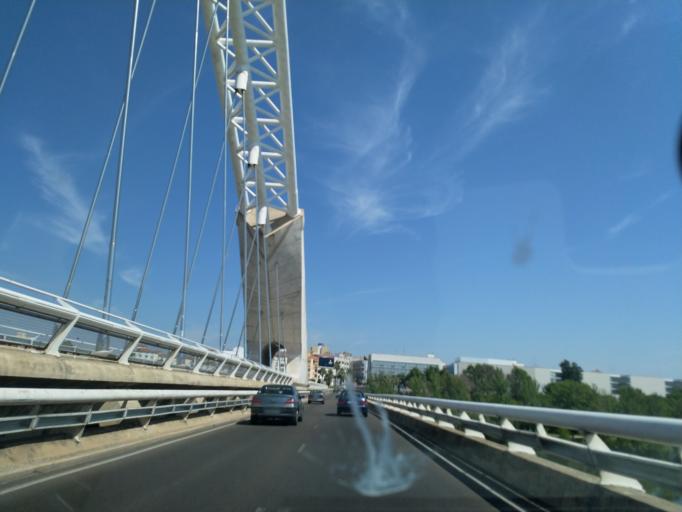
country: ES
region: Extremadura
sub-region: Provincia de Badajoz
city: Merida
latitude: 38.9168
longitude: -6.3534
